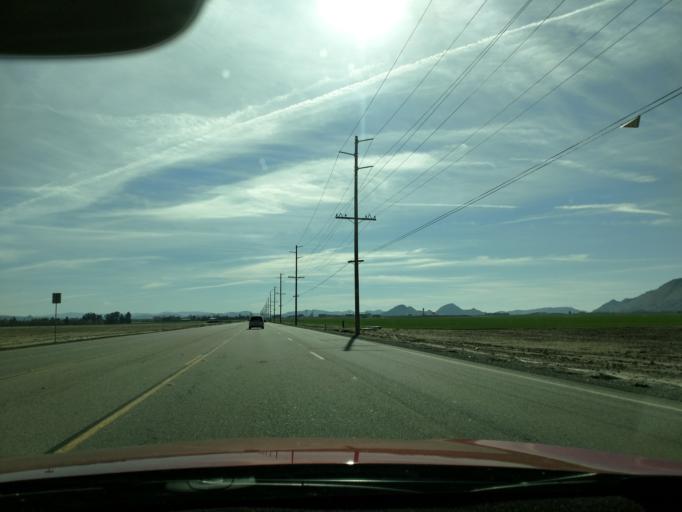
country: US
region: California
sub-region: Riverside County
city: San Jacinto
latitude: 33.8136
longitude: -117.0070
